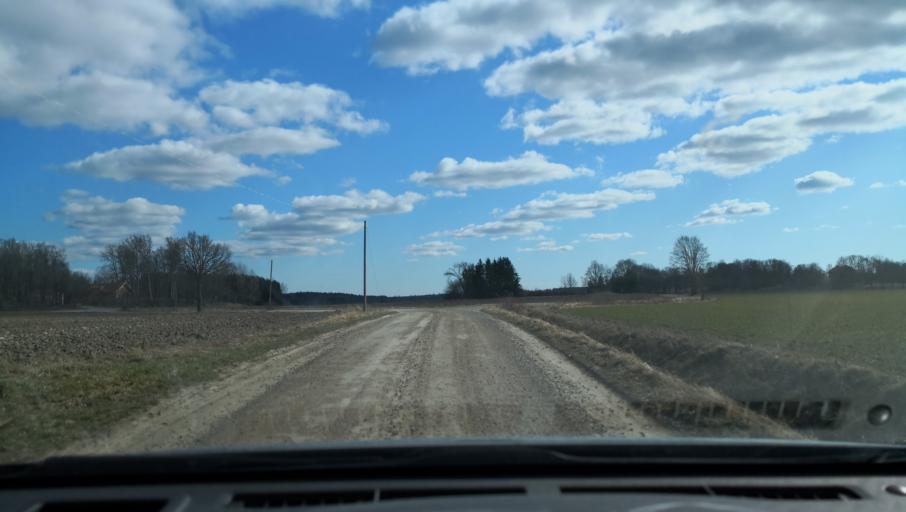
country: SE
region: Soedermanland
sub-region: Katrineholms Kommun
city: Katrineholm
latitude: 59.1433
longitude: 16.0776
